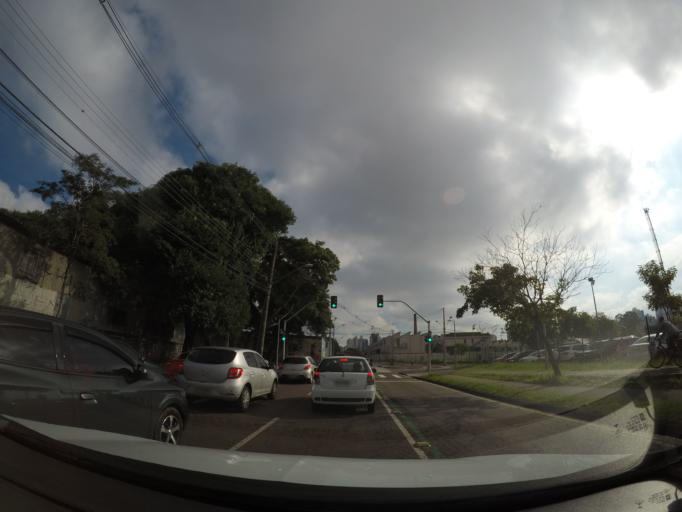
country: BR
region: Parana
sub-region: Curitiba
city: Curitiba
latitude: -25.4409
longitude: -49.2602
